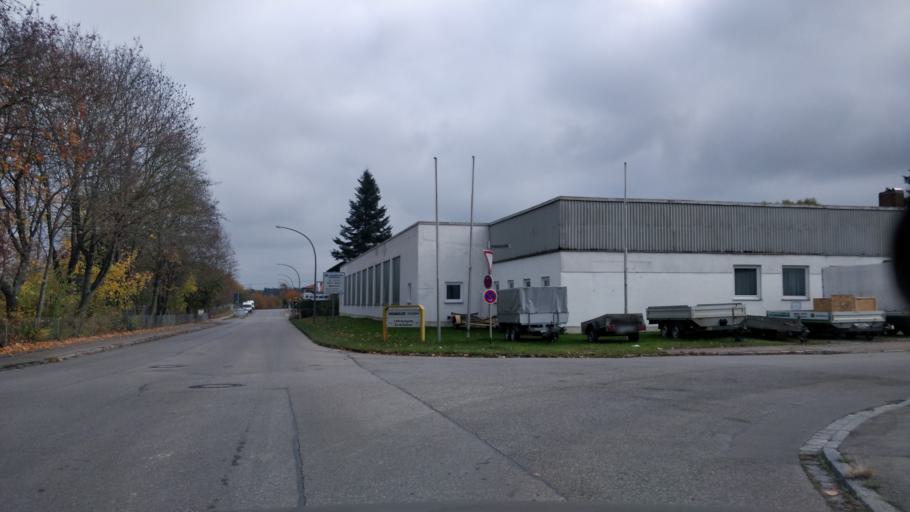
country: DE
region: Bavaria
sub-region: Swabia
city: Friedberg
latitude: 48.3504
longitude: 10.9950
